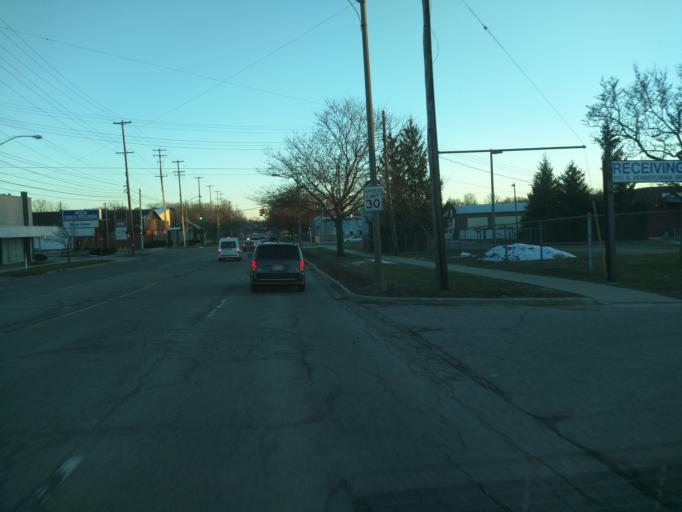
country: US
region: Michigan
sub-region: Ingham County
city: Lansing
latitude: 42.7224
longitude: -84.5382
